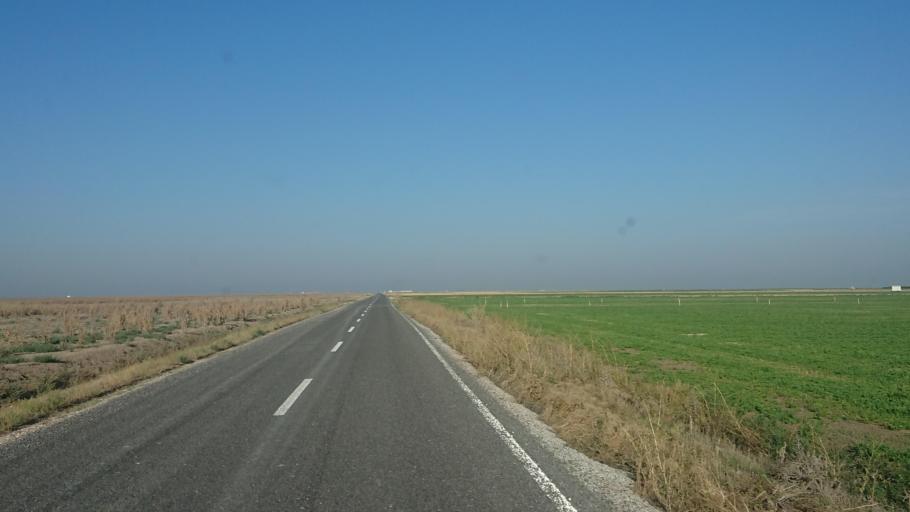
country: TR
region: Aksaray
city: Yesilova
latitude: 38.3876
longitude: 33.7785
